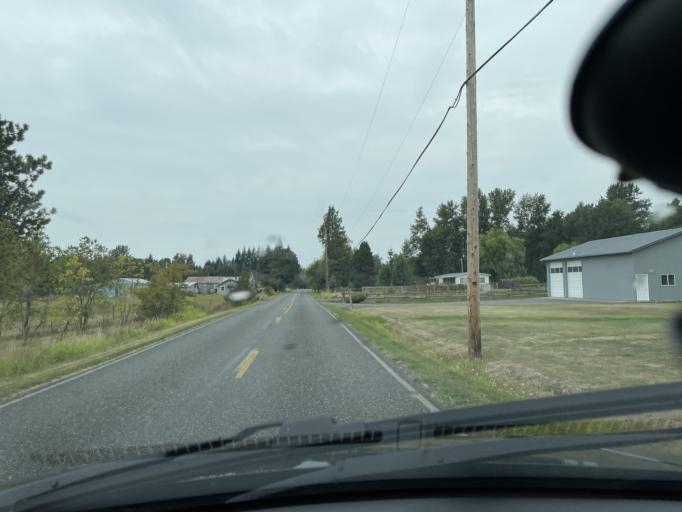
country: US
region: Washington
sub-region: Whatcom County
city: Marietta-Alderwood
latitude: 48.8261
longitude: -122.5276
